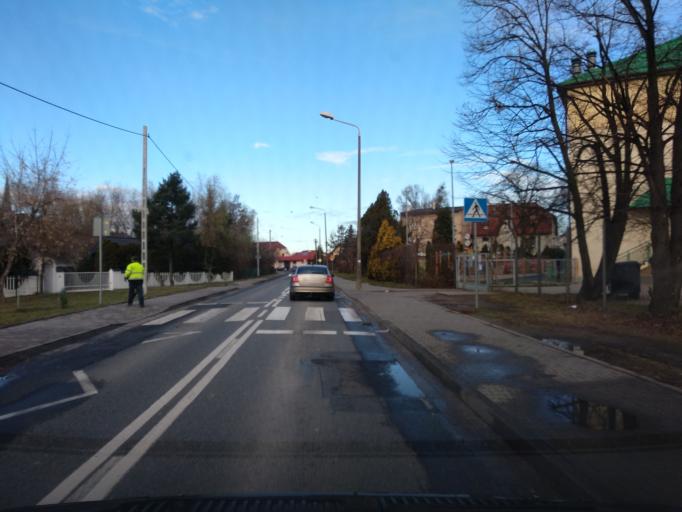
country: PL
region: Lower Silesian Voivodeship
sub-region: Powiat wroclawski
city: Zerniki Wroclawskie
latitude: 51.0552
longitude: 17.0265
